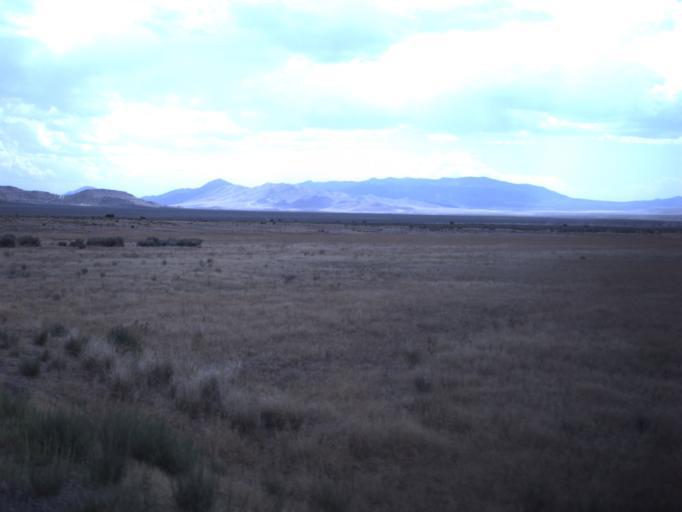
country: US
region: Utah
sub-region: Utah County
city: Eagle Mountain
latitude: 40.2408
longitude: -112.2052
